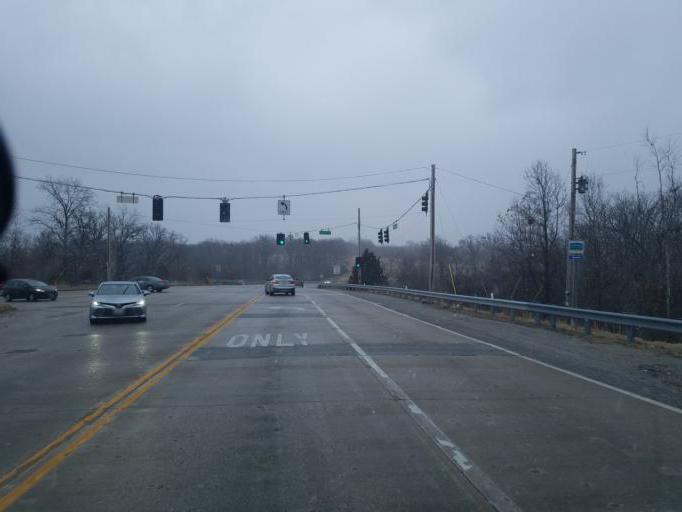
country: US
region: Missouri
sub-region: Boone County
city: Columbia
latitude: 38.9463
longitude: -92.2917
